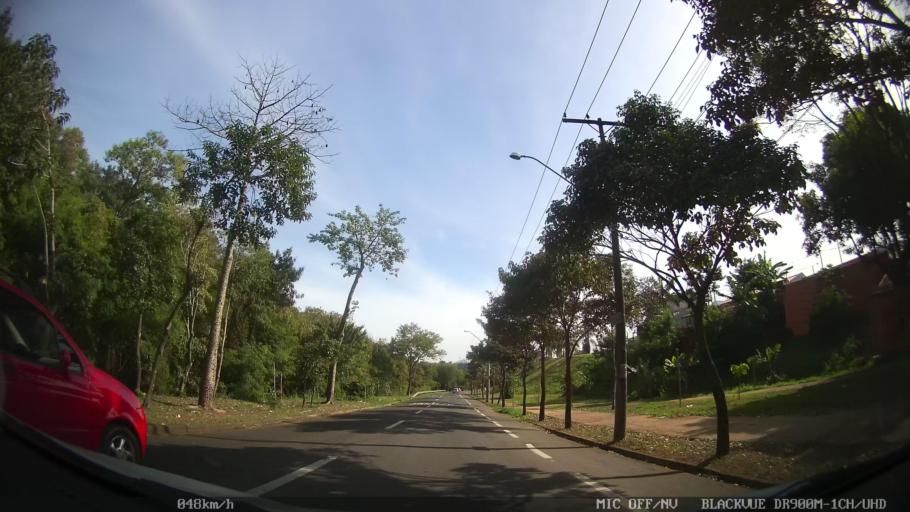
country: BR
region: Sao Paulo
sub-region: Piracicaba
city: Piracicaba
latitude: -22.7331
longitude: -47.6709
